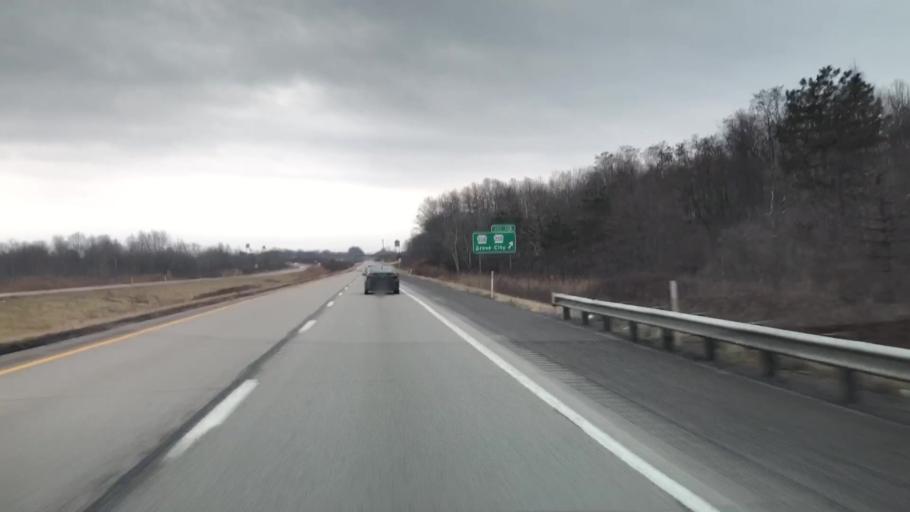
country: US
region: Pennsylvania
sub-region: Mercer County
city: Grove City
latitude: 41.1520
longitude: -80.1564
